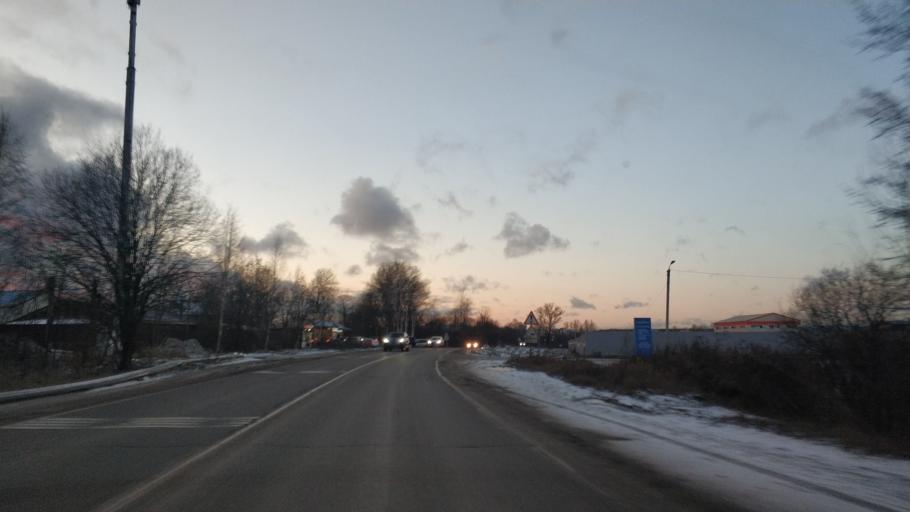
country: RU
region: St.-Petersburg
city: Pontonnyy
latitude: 59.8072
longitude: 30.6193
